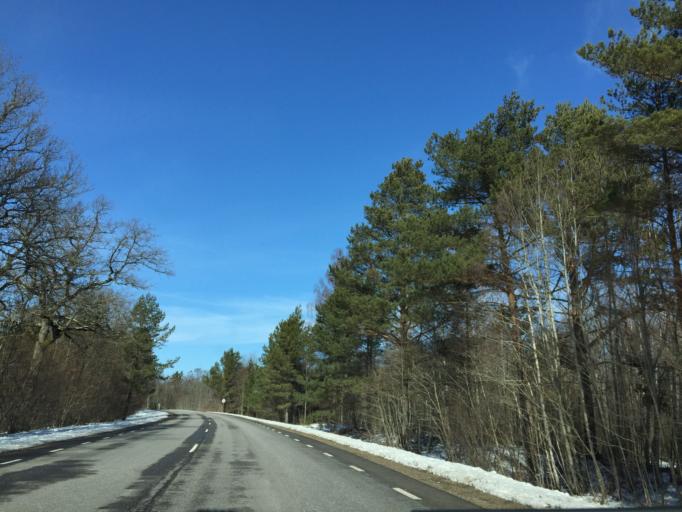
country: EE
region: Laeaene
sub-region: Lihula vald
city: Lihula
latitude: 58.6116
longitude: 23.6951
